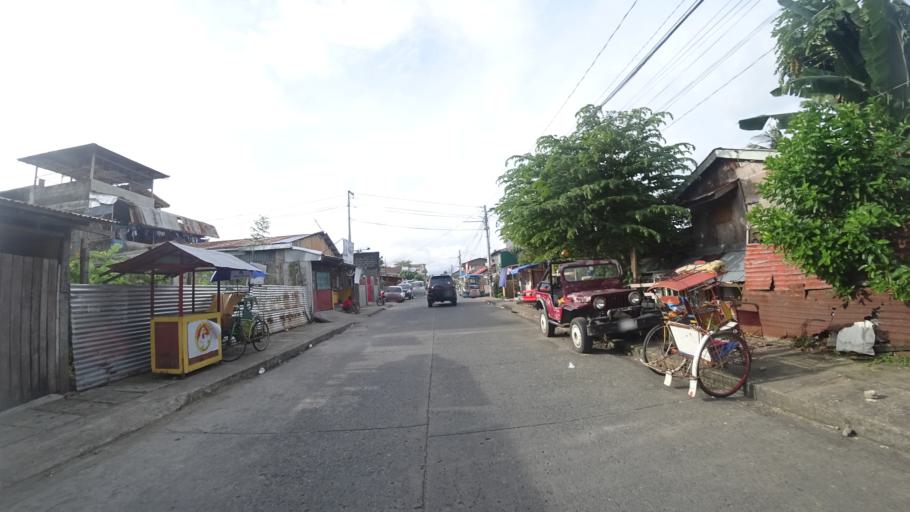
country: PH
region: Eastern Visayas
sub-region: Province of Leyte
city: Panalanoy
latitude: 11.2350
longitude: 125.0046
